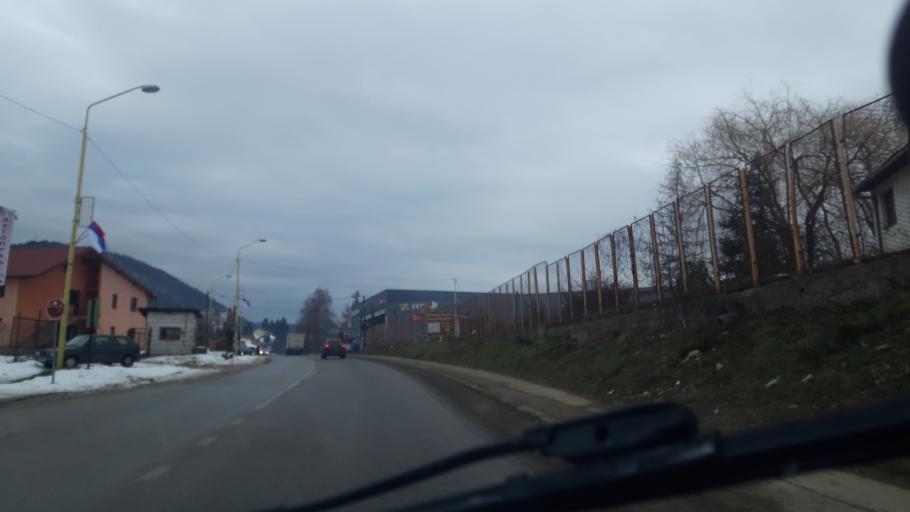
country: BA
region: Republika Srpska
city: Vlasenica
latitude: 44.1839
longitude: 18.9458
